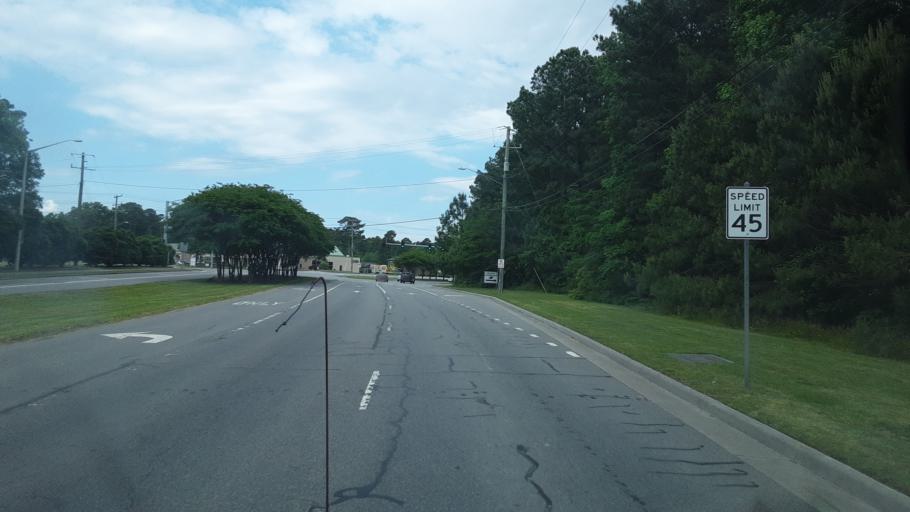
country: US
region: Virginia
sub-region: City of Virginia Beach
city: Virginia Beach
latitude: 36.7942
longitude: -75.9967
